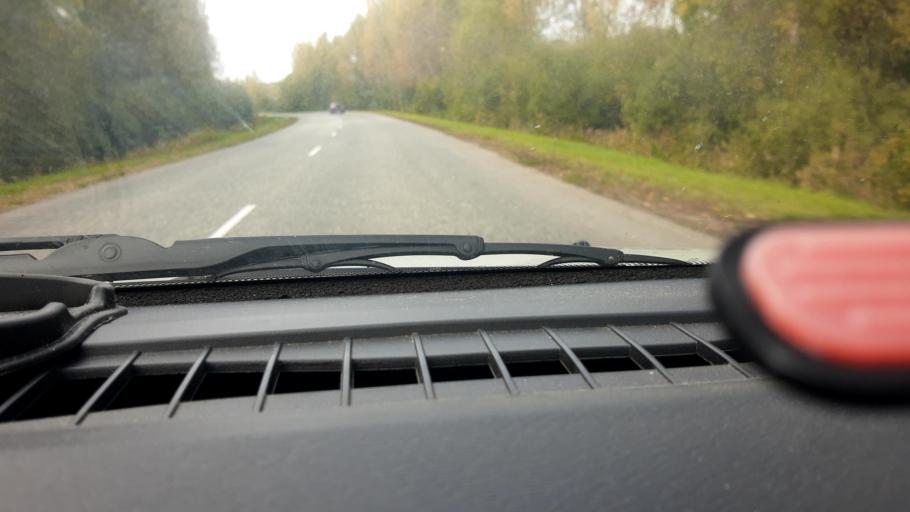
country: RU
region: Nizjnij Novgorod
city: Prudy
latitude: 57.3665
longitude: 46.1789
